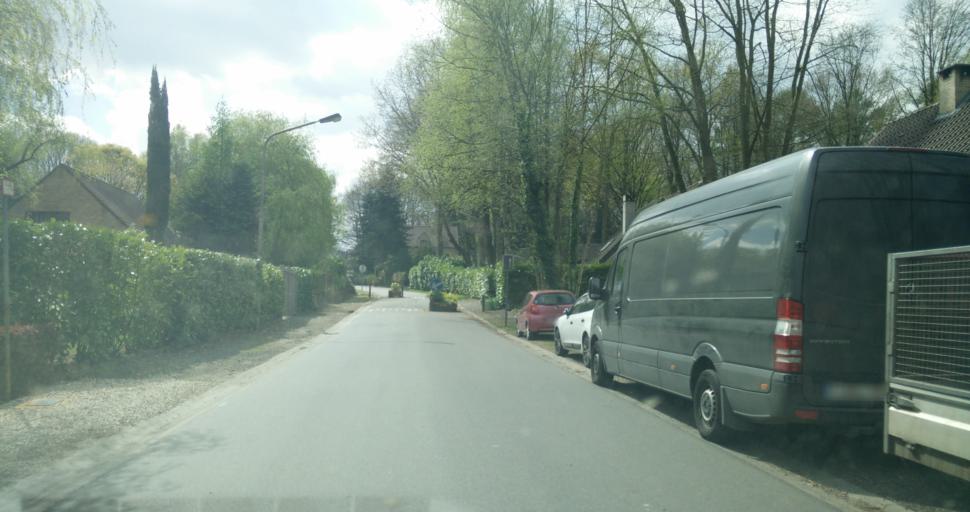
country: BE
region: Wallonia
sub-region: Province du Brabant Wallon
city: Tubize
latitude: 50.6381
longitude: 4.1954
